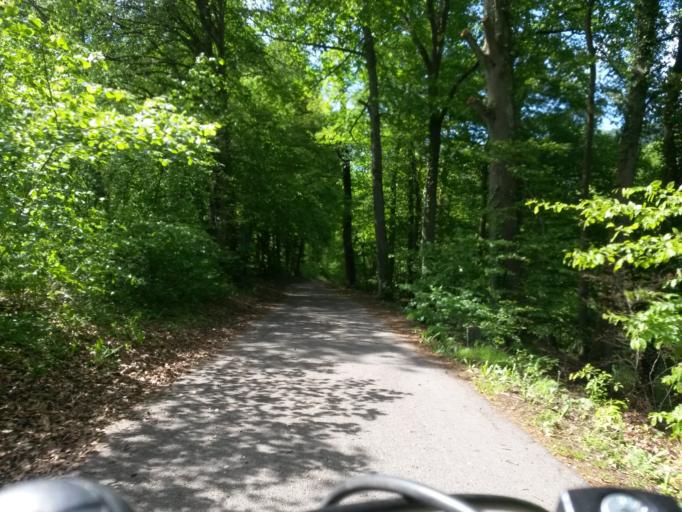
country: DE
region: Baden-Wuerttemberg
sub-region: Karlsruhe Region
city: Bad Liebenzell
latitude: 48.7945
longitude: 8.7288
